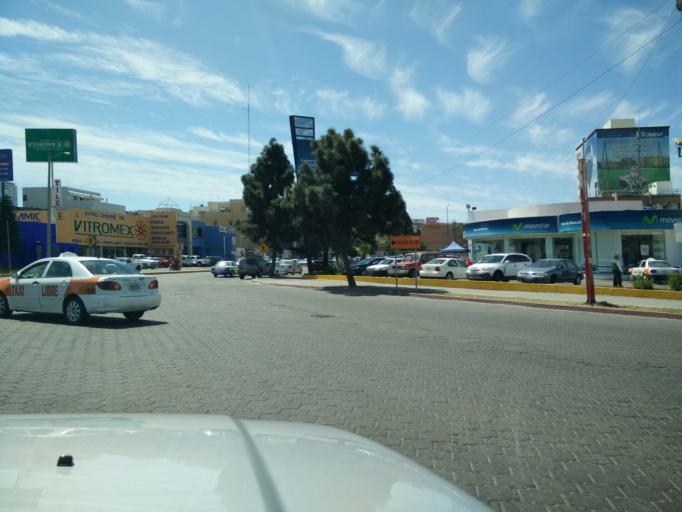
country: MX
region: Baja California
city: Tijuana
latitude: 32.5205
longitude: -117.0107
